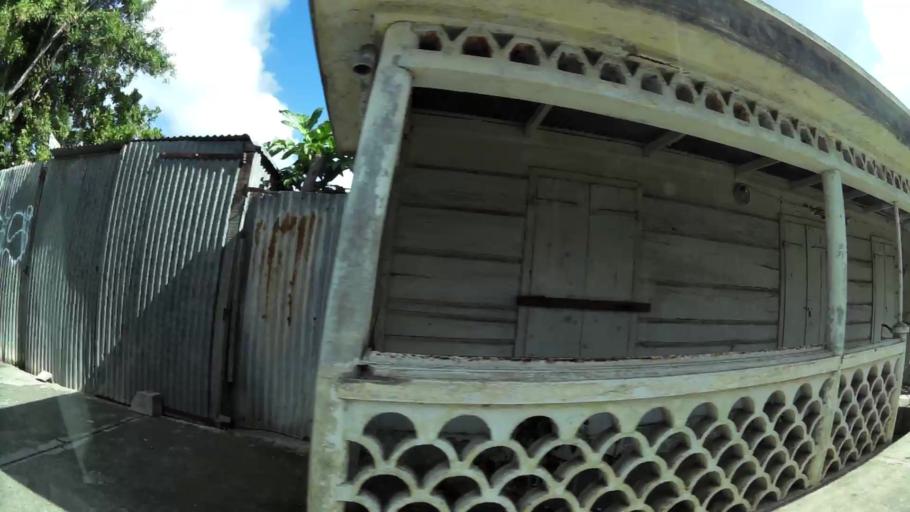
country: GP
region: Guadeloupe
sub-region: Guadeloupe
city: Saint-Francois
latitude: 16.2537
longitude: -61.2719
